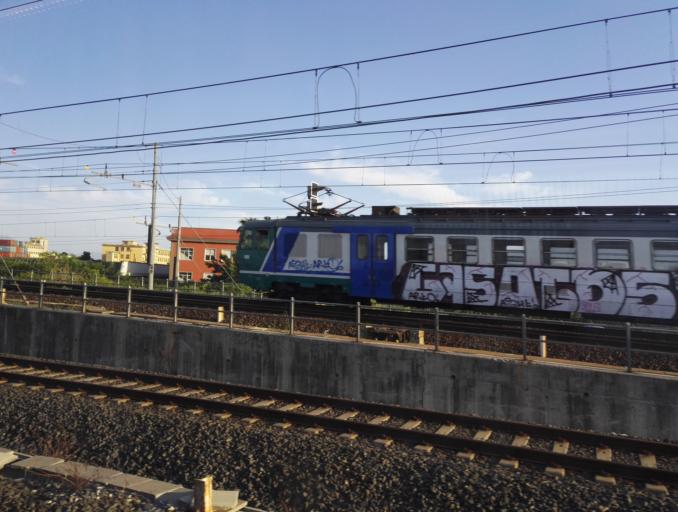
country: IT
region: Campania
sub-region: Provincia di Napoli
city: Napoli
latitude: 40.8538
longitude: 14.2904
